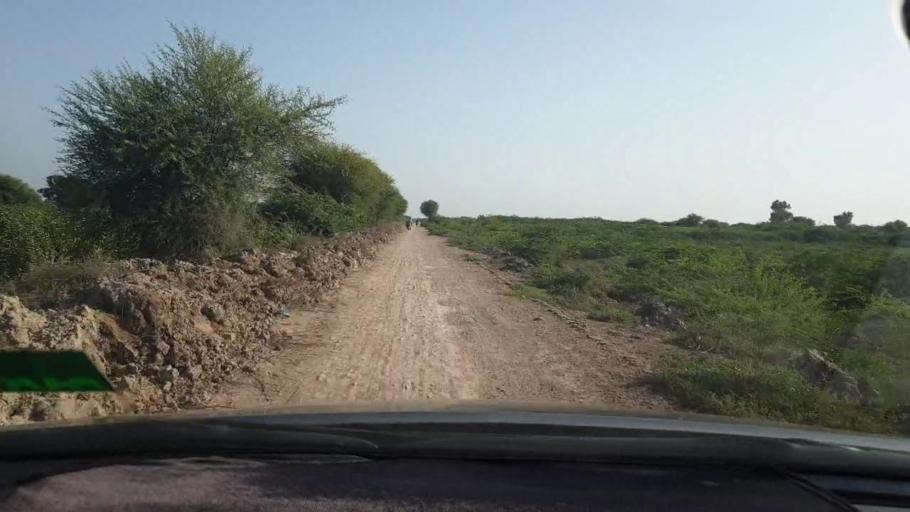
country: PK
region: Sindh
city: Naukot
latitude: 24.9132
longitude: 69.2766
